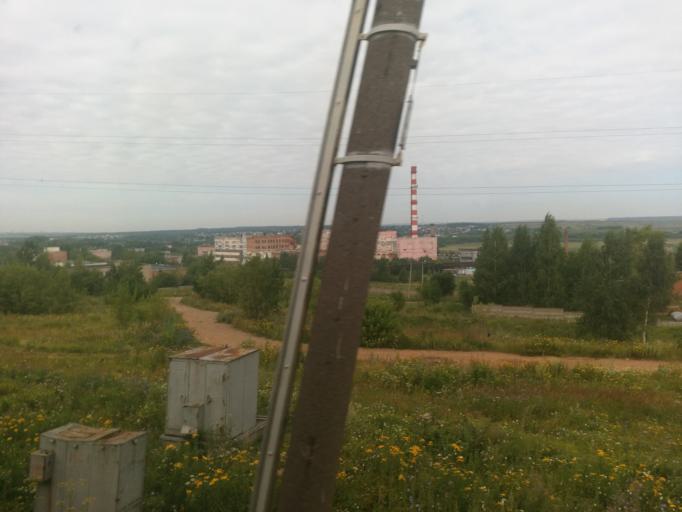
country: RU
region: Tatarstan
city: Mendeleyevsk
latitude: 55.8992
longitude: 52.3296
